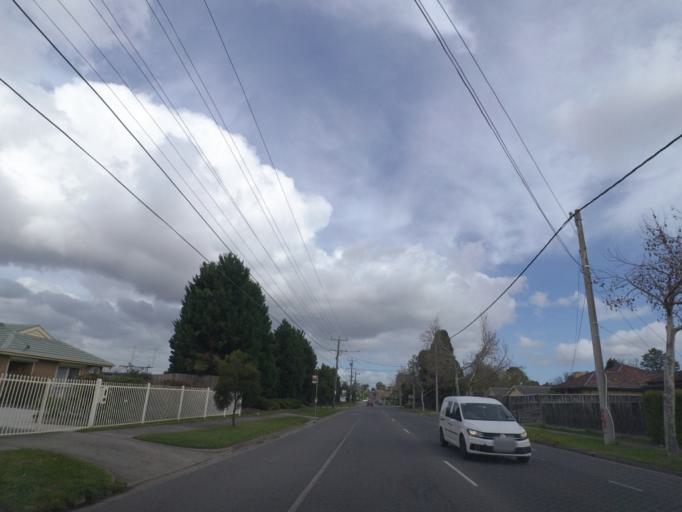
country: AU
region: Victoria
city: Mitcham
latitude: -37.8299
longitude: 145.2134
